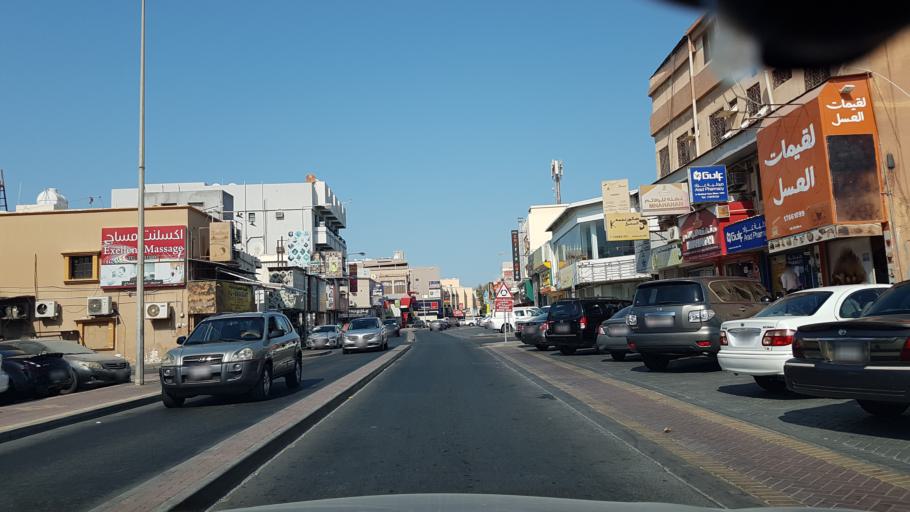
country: BH
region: Muharraq
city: Al Muharraq
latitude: 26.2556
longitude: 50.6329
